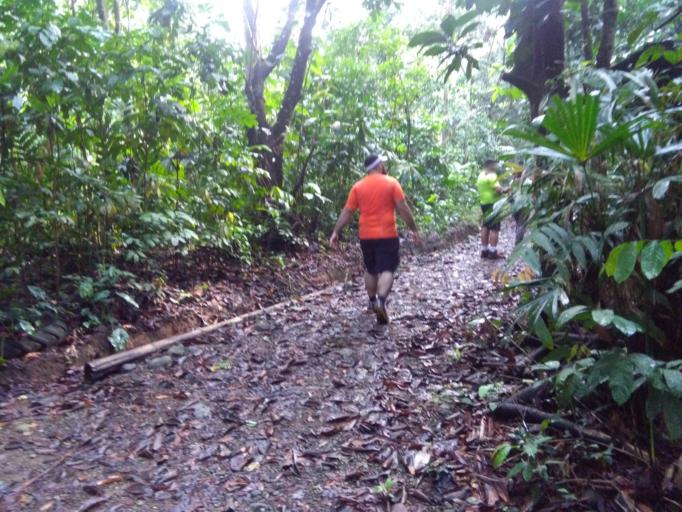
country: CR
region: Puntarenas
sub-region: Canton de Golfito
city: Golfito
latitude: 8.6545
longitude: -83.1784
